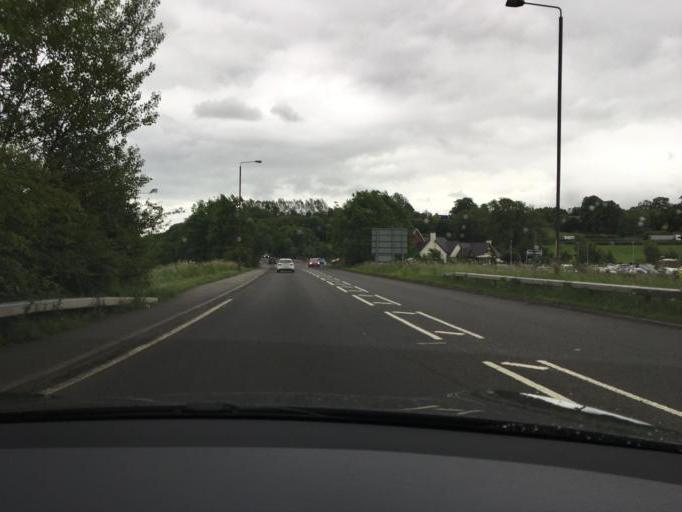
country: GB
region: England
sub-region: Derbyshire
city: Ashbourne
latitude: 53.0102
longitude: -1.7481
